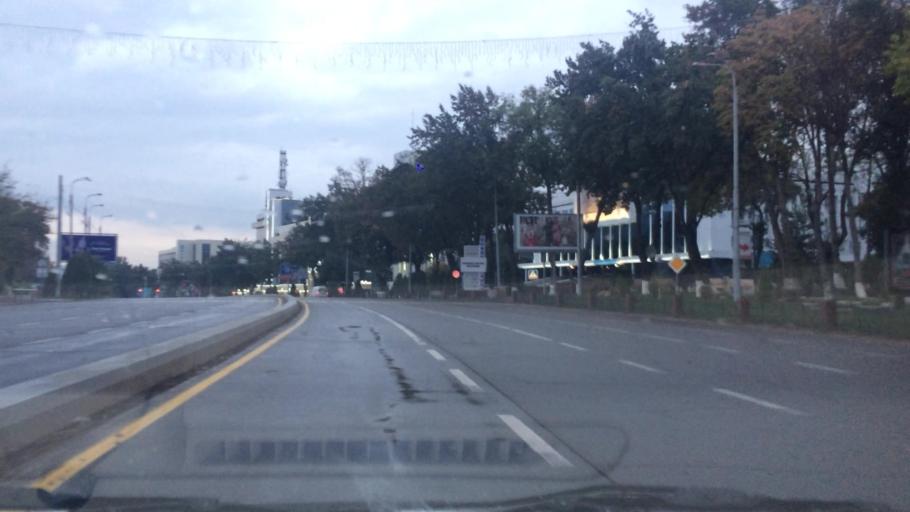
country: UZ
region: Toshkent Shahri
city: Tashkent
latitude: 41.3154
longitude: 69.2848
